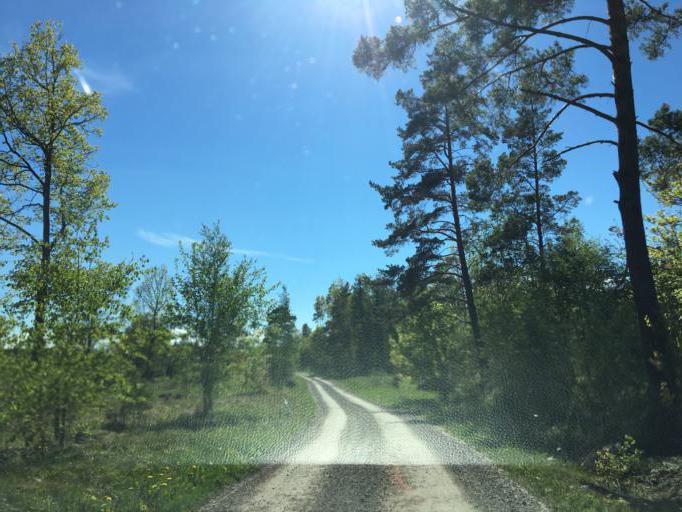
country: SE
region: Soedermanland
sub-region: Eskilstuna Kommun
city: Kvicksund
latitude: 59.3450
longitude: 16.3079
